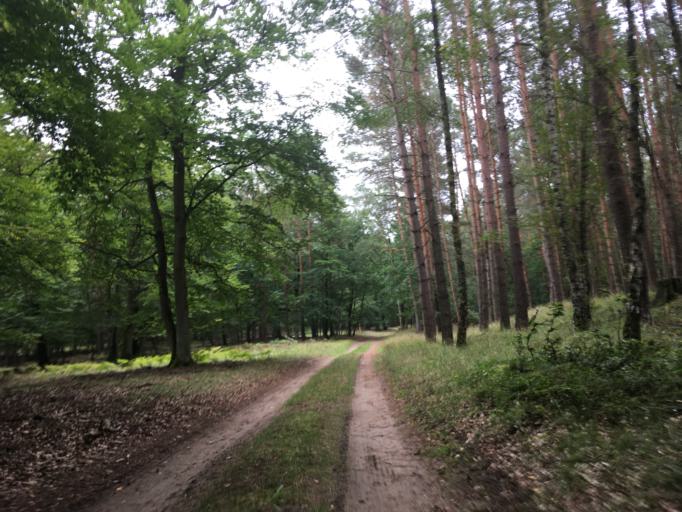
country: DE
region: Brandenburg
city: Zehdenick
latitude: 53.0410
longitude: 13.3308
